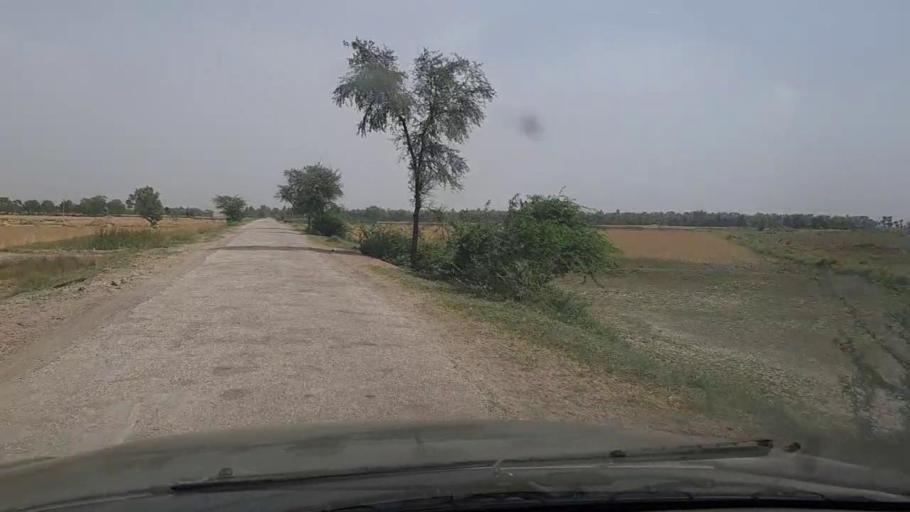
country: PK
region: Sindh
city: Lakhi
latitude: 27.8475
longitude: 68.7553
